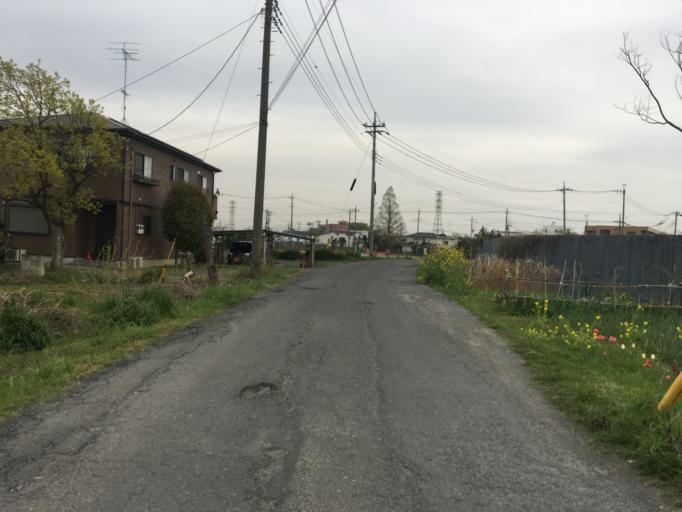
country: JP
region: Saitama
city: Shiki
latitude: 35.8460
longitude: 139.5773
